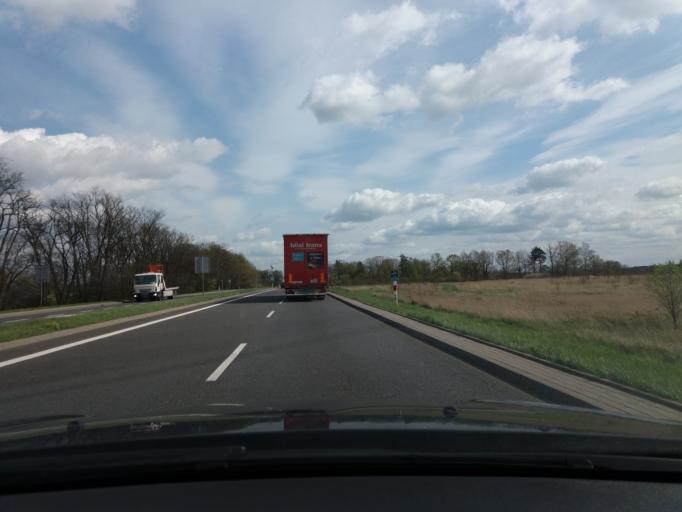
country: PL
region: Lower Silesian Voivodeship
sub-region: Powiat sredzki
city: Malczyce
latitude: 51.2175
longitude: 16.4531
